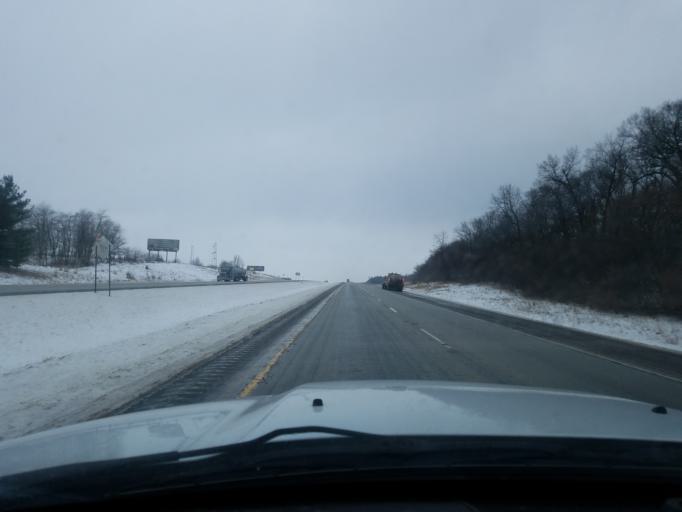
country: US
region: Indiana
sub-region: Fulton County
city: Rochester
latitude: 41.1146
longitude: -86.2397
